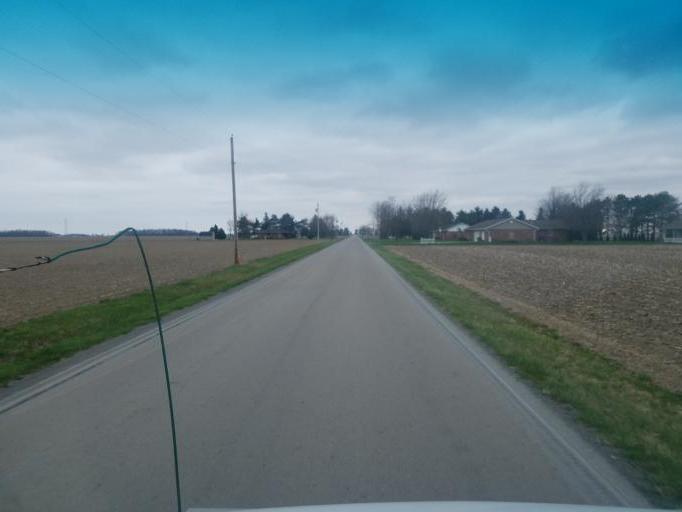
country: US
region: Ohio
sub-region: Allen County
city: Delphos
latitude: 40.9180
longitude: -84.3628
